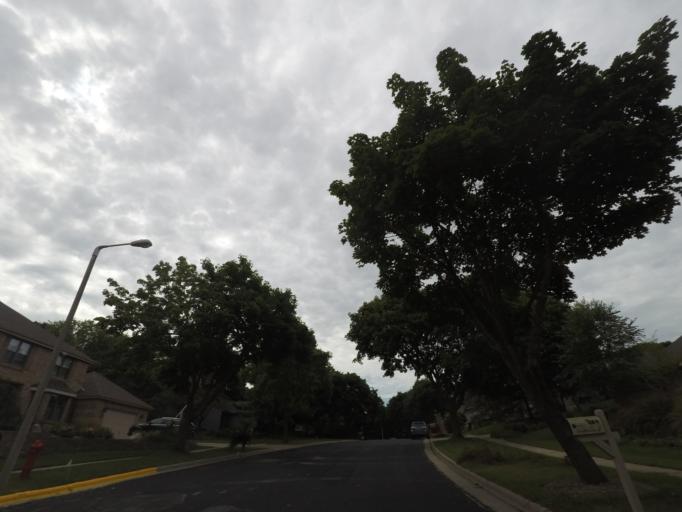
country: US
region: Wisconsin
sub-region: Dane County
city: Middleton
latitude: 43.0853
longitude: -89.4929
